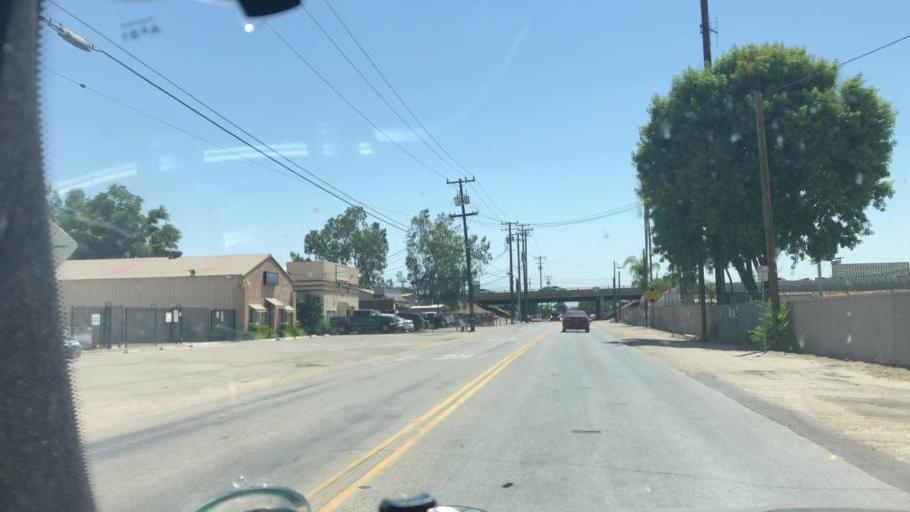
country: US
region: California
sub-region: Kern County
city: Bakersfield
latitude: 35.3894
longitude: -119.0467
